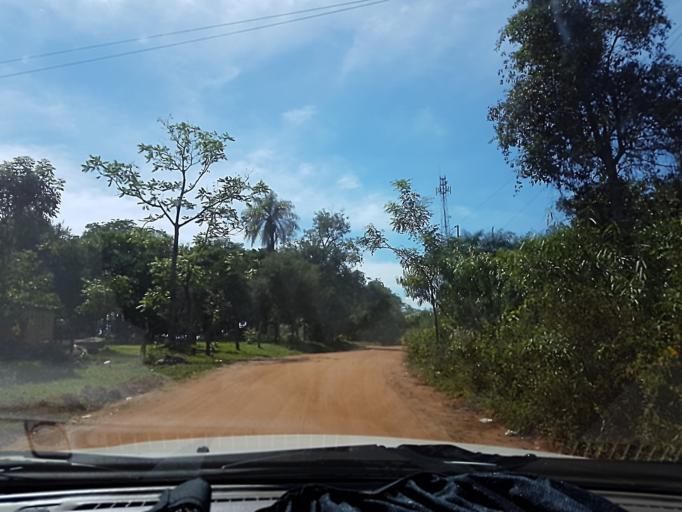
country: PY
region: Cordillera
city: Arroyos y Esteros
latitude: -24.9922
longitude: -57.2134
